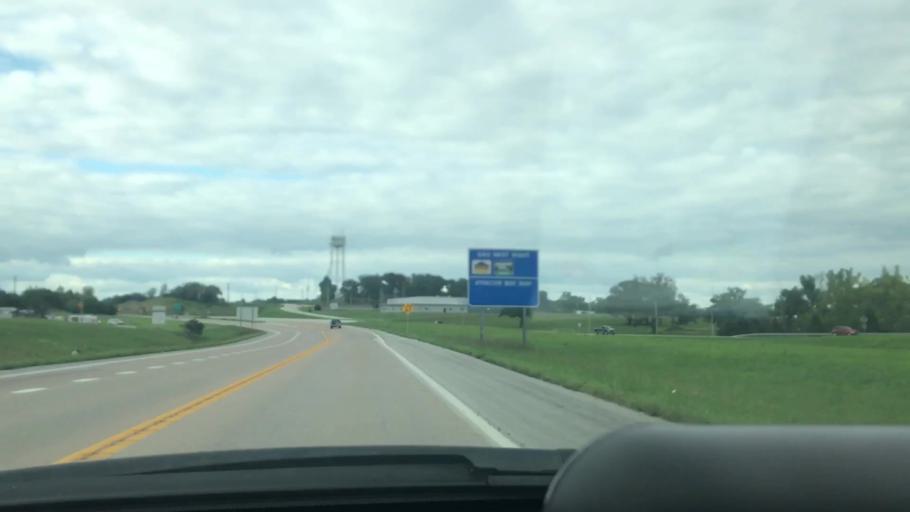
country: US
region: Missouri
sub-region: Benton County
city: Warsaw
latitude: 38.2438
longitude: -93.3603
